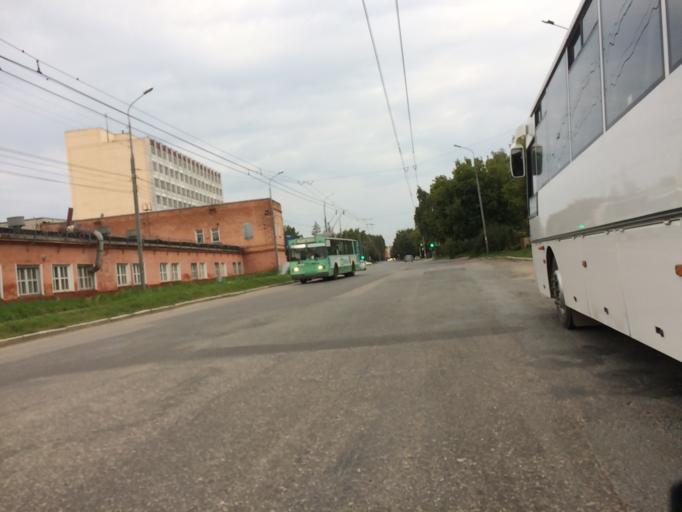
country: RU
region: Mariy-El
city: Yoshkar-Ola
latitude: 56.6333
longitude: 47.8688
